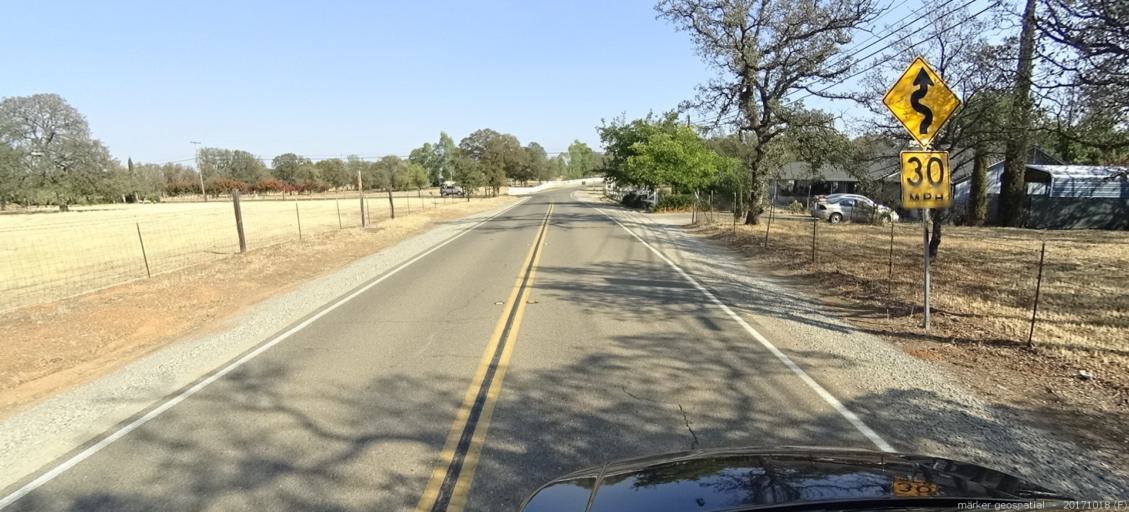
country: US
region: California
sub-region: Shasta County
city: Palo Cedro
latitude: 40.5639
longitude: -122.2636
